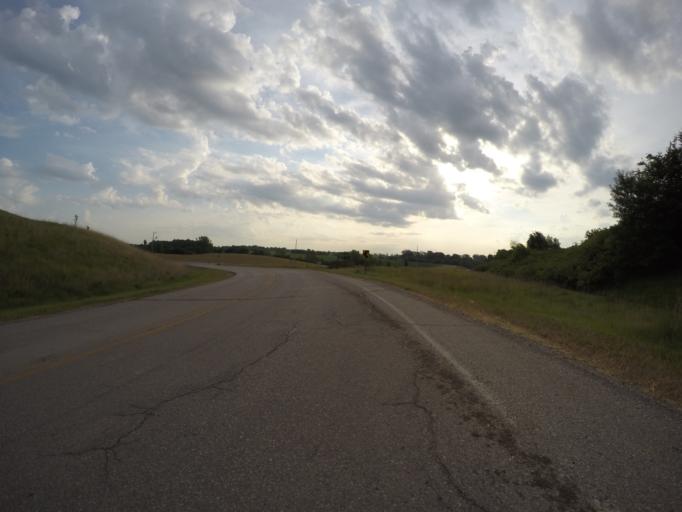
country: US
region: Kansas
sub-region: Doniphan County
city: Troy
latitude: 39.7918
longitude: -95.0759
